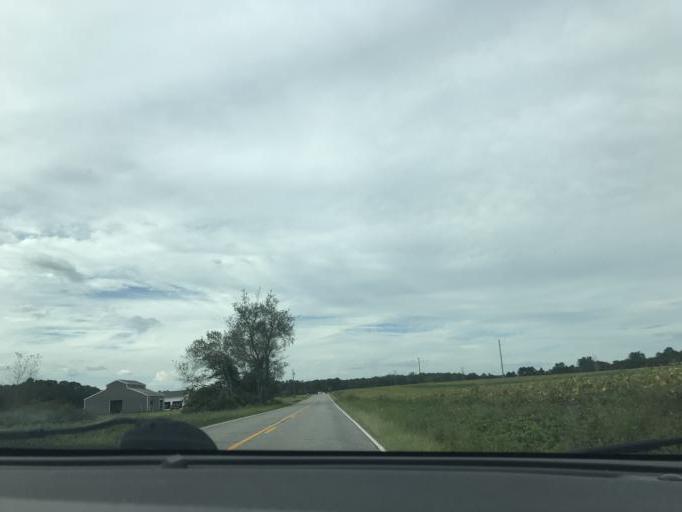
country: US
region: South Carolina
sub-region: Cherokee County
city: Gaffney
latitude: 35.1495
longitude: -81.6970
